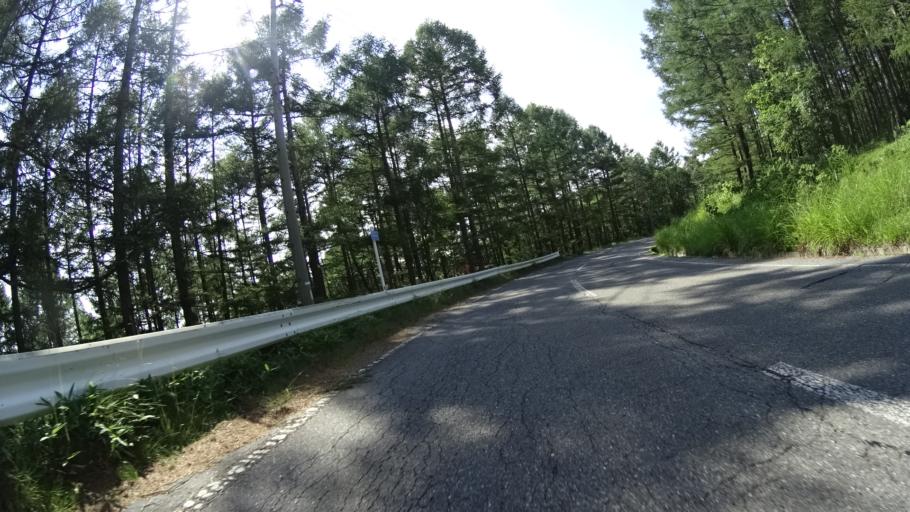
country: JP
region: Nagano
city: Chino
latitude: 36.0459
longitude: 138.3080
